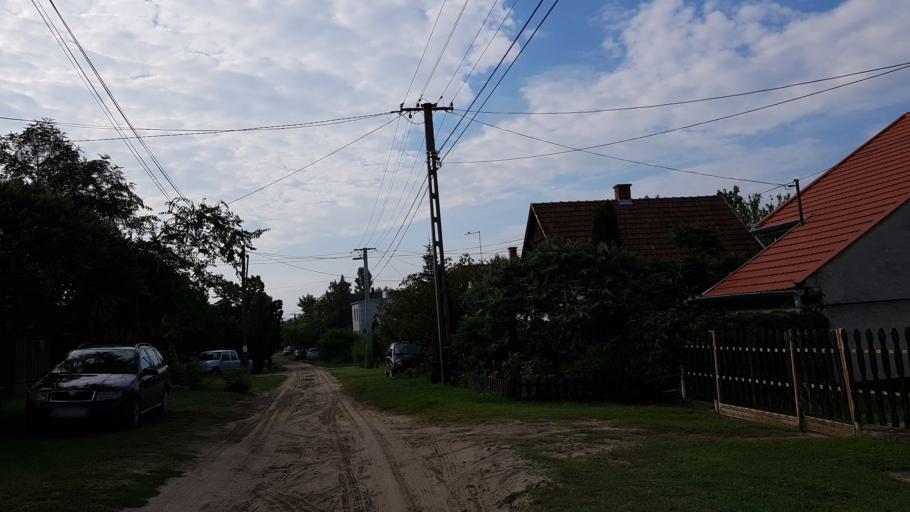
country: HU
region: Bacs-Kiskun
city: Lakitelek
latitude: 46.8659
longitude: 19.9953
